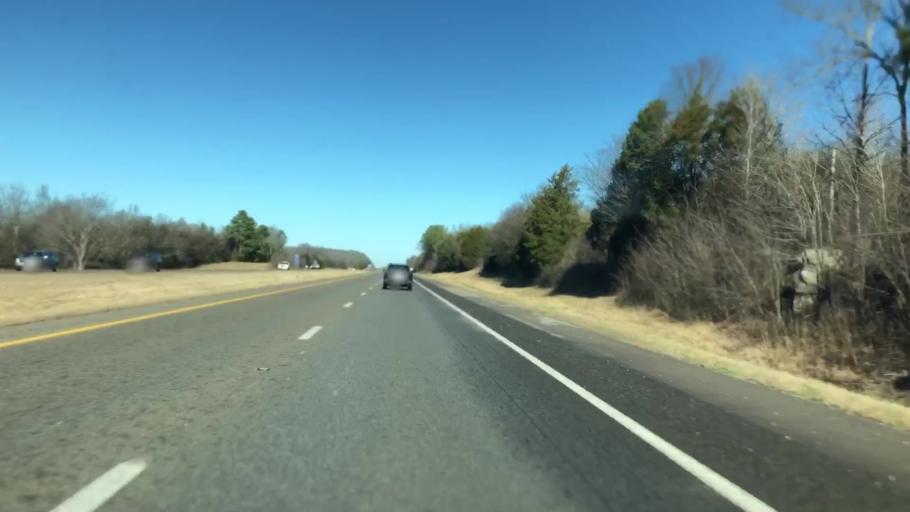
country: US
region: Tennessee
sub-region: Marshall County
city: Lewisburg
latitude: 35.5239
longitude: -86.8996
